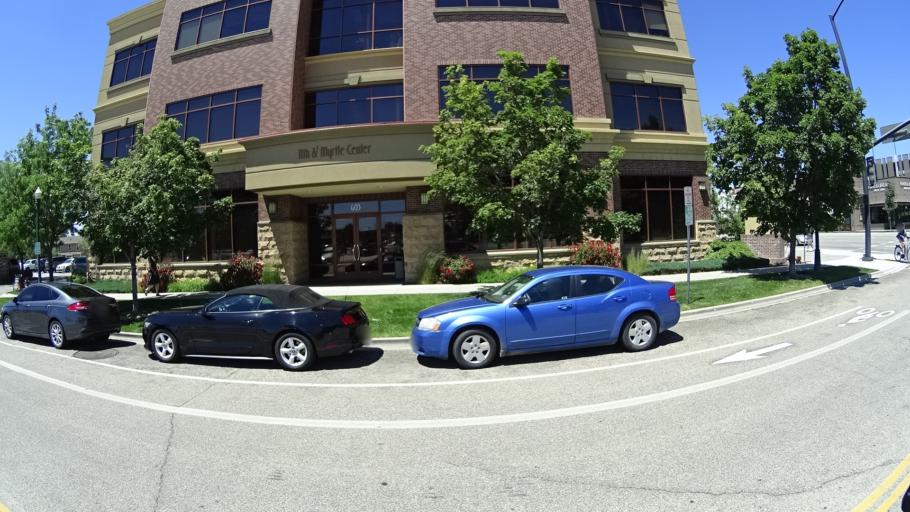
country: US
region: Idaho
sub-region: Ada County
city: Boise
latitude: 43.6145
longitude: -116.2088
